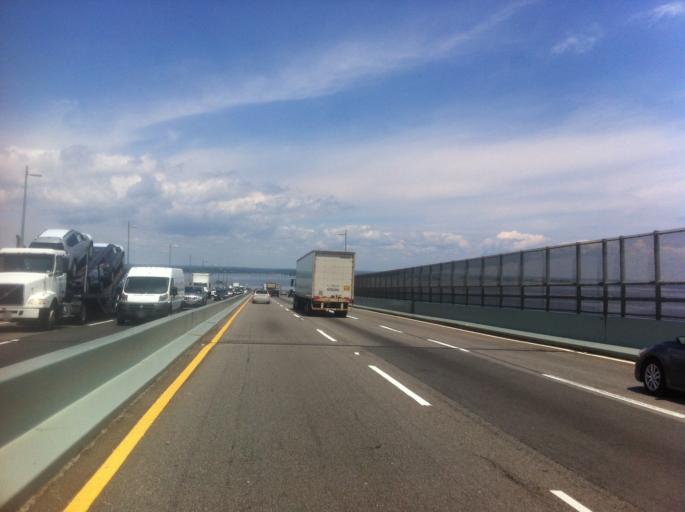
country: US
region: New York
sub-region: Nassau County
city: East Atlantic Beach
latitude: 40.7996
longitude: -73.7936
